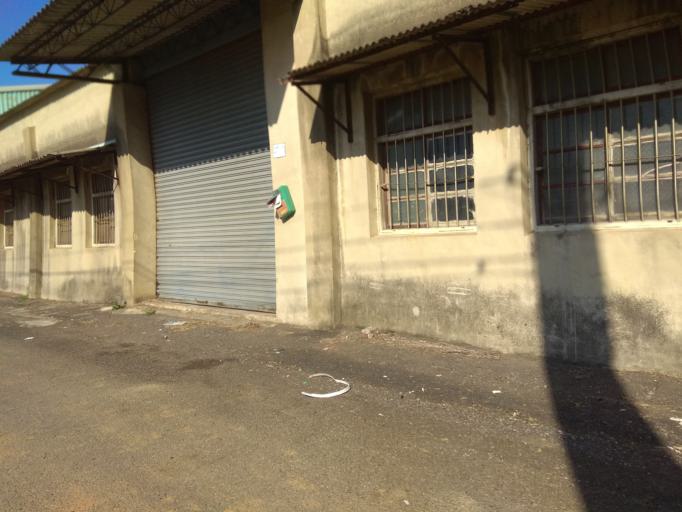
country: TW
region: Taiwan
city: Taoyuan City
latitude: 25.0446
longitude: 121.2227
